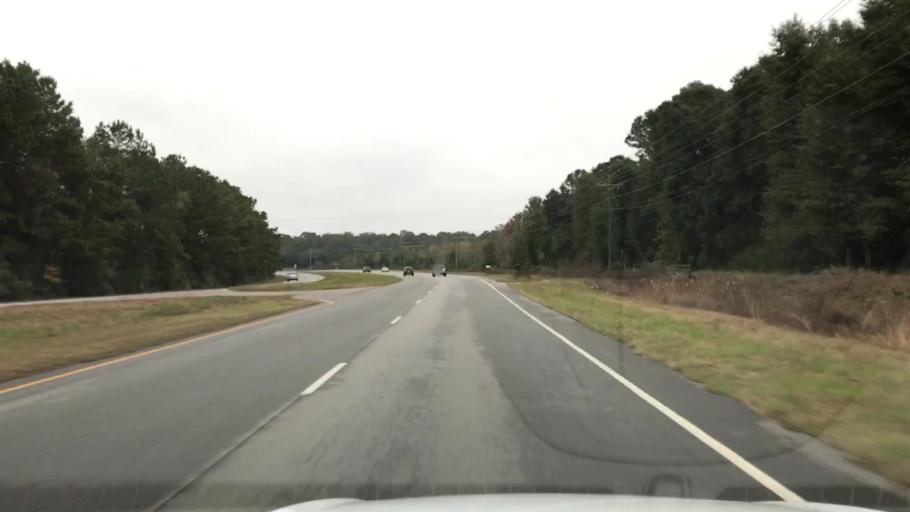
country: US
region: South Carolina
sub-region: Charleston County
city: Isle of Palms
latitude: 32.9171
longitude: -79.7175
